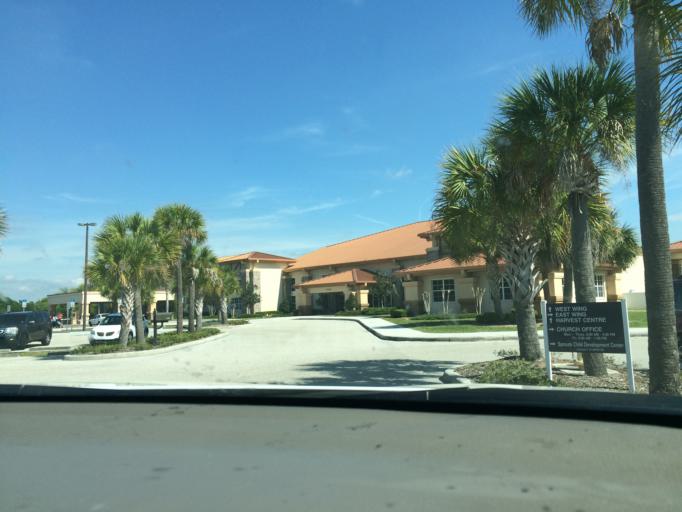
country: US
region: Florida
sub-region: Sarasota County
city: The Meadows
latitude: 27.3917
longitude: -82.3967
